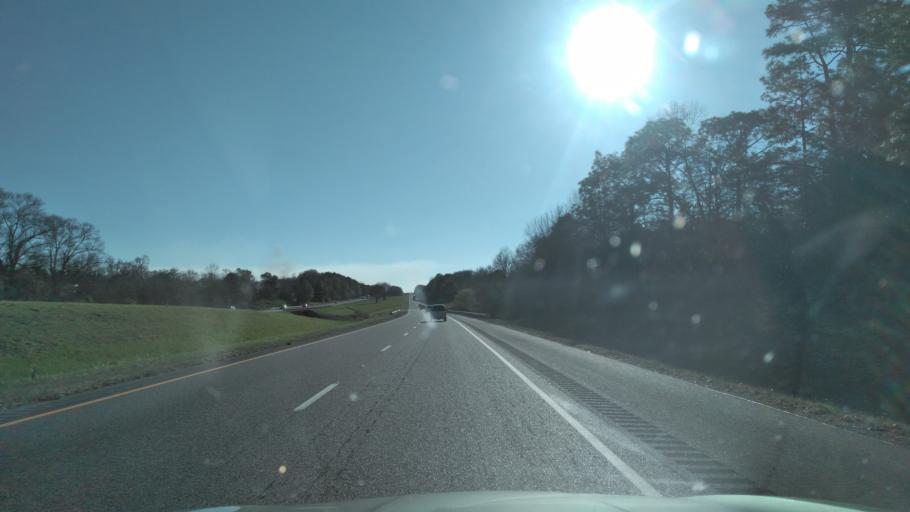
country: US
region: Alabama
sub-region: Escambia County
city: Atmore
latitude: 31.0988
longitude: -87.5135
